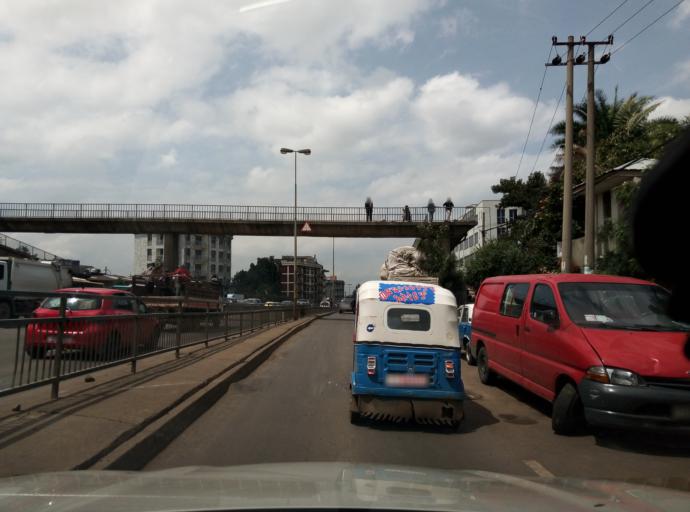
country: ET
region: Adis Abeba
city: Addis Ababa
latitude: 9.0004
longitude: 38.7189
